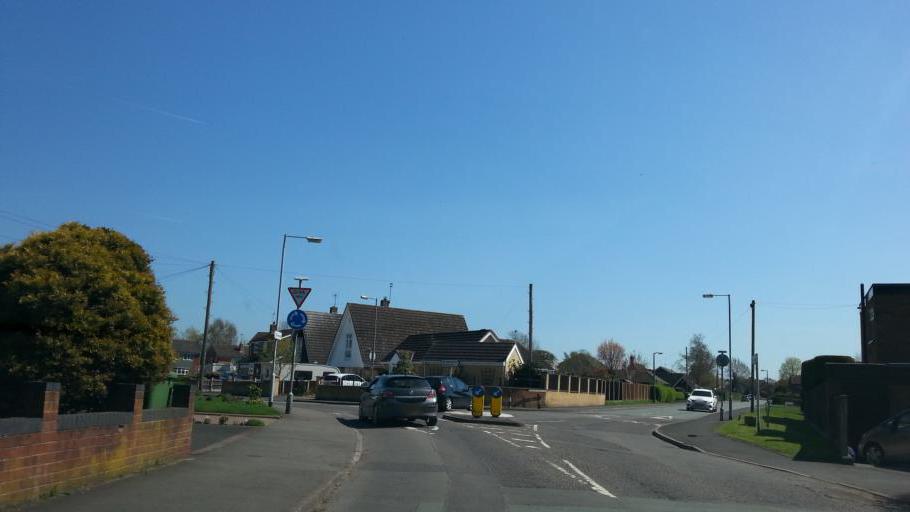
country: GB
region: England
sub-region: Staffordshire
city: Brewood
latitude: 52.6609
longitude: -2.1412
